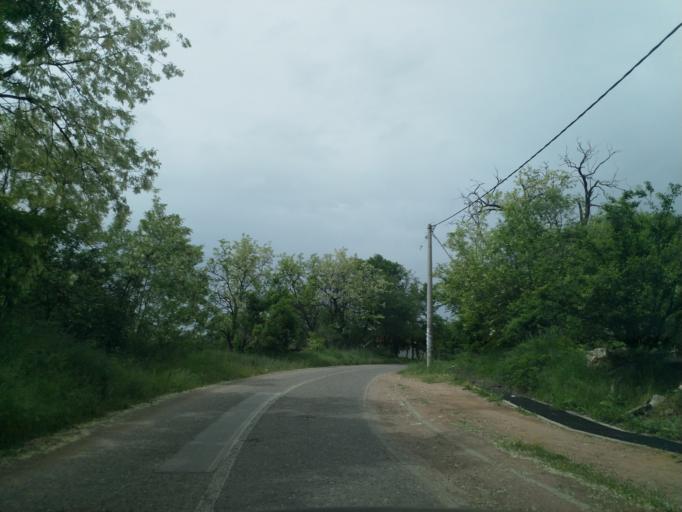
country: RS
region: Central Serbia
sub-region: Pomoravski Okrug
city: Paracin
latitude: 43.8609
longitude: 21.5891
